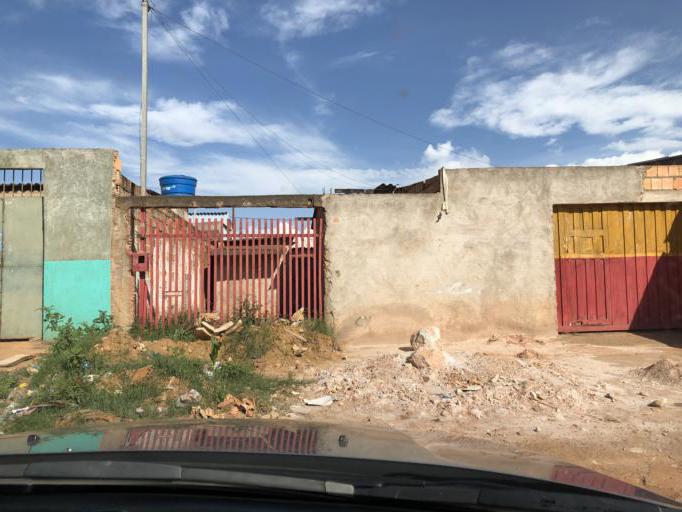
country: BR
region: Federal District
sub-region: Brasilia
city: Brasilia
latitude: -15.8207
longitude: -48.1547
